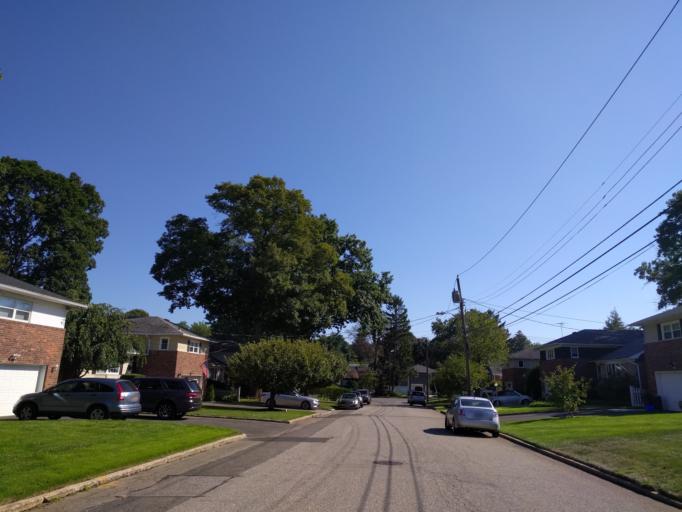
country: US
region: New York
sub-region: Nassau County
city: Locust Valley
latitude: 40.8757
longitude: -73.6171
